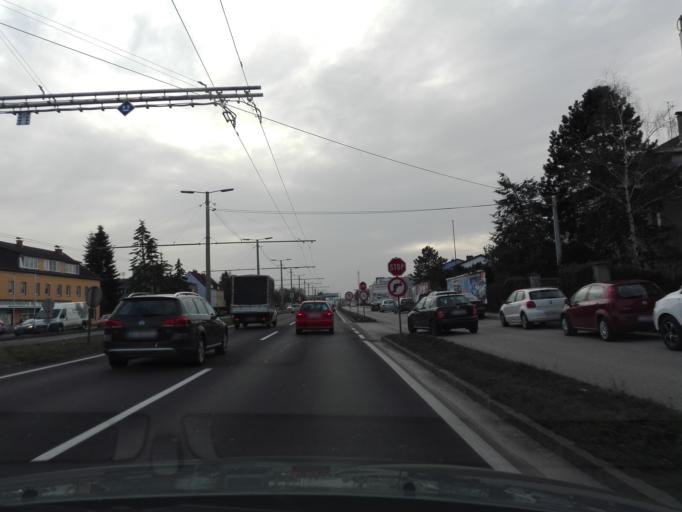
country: AT
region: Upper Austria
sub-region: Politischer Bezirk Linz-Land
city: Traun
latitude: 48.2428
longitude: 14.2541
